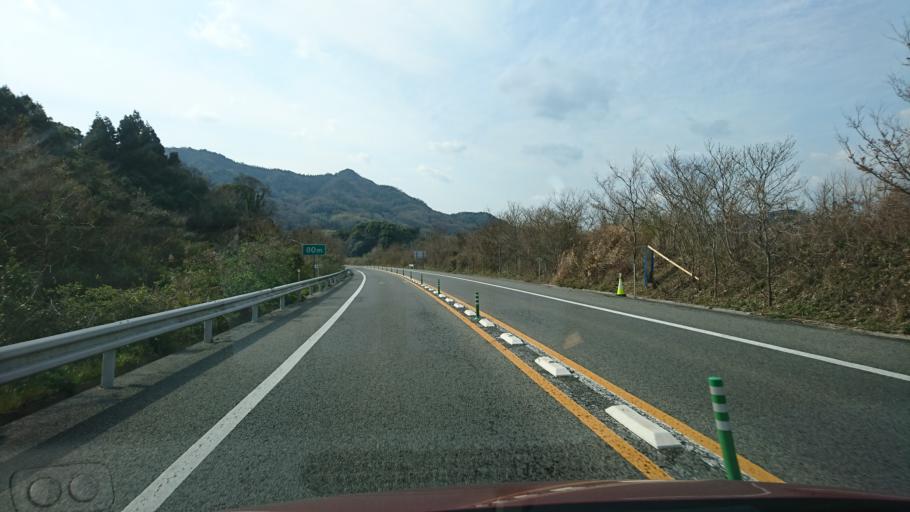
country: JP
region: Hiroshima
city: Innoshima
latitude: 34.1320
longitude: 133.0451
